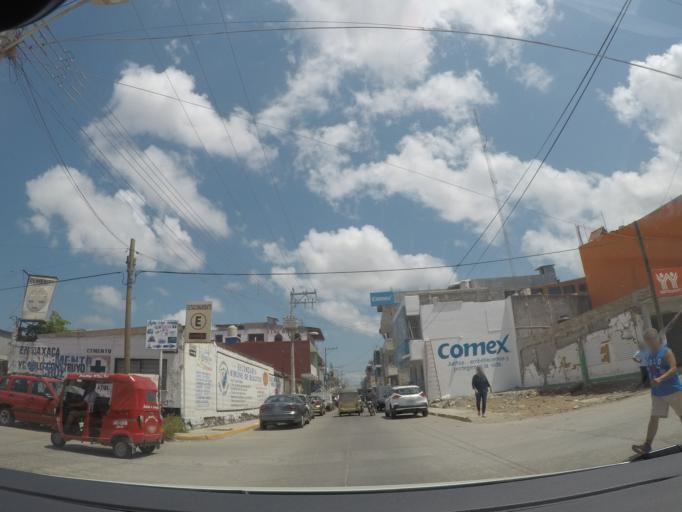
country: MX
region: Oaxaca
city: Juchitan de Zaragoza
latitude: 16.4361
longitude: -95.0224
